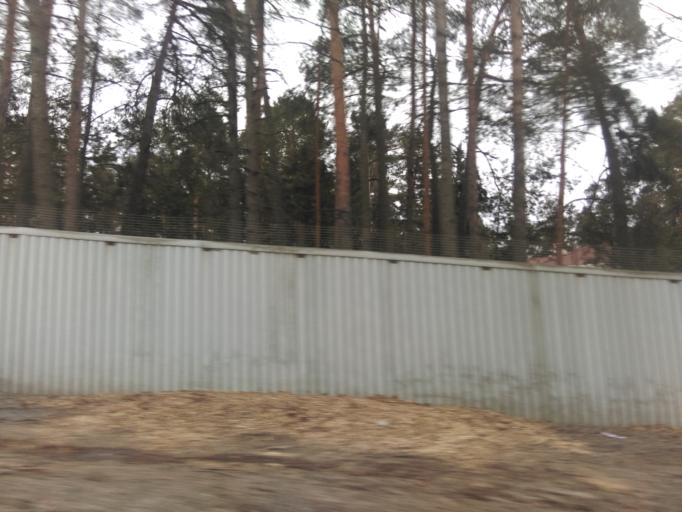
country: RU
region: Moskovskaya
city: Barvikha
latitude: 55.7441
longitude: 37.2863
